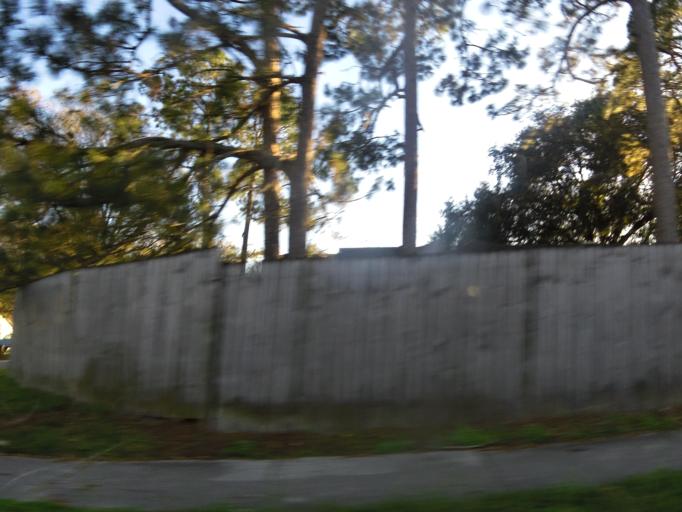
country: US
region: Florida
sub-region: Saint Johns County
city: Fruit Cove
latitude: 30.1723
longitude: -81.5791
